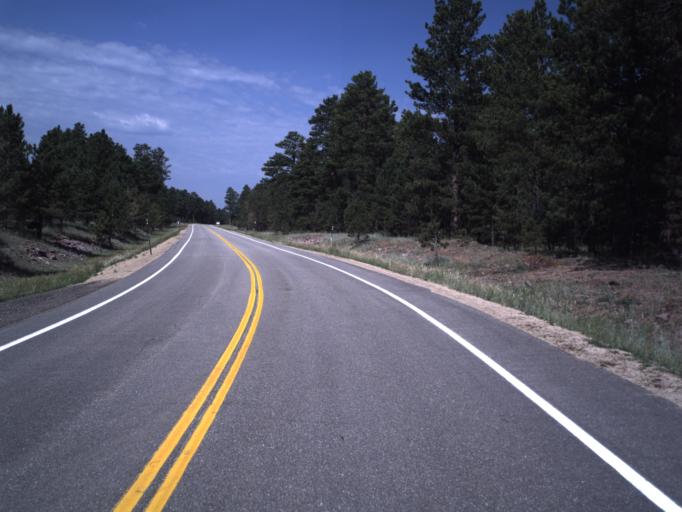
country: US
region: Utah
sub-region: Daggett County
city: Manila
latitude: 40.8531
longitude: -109.5933
